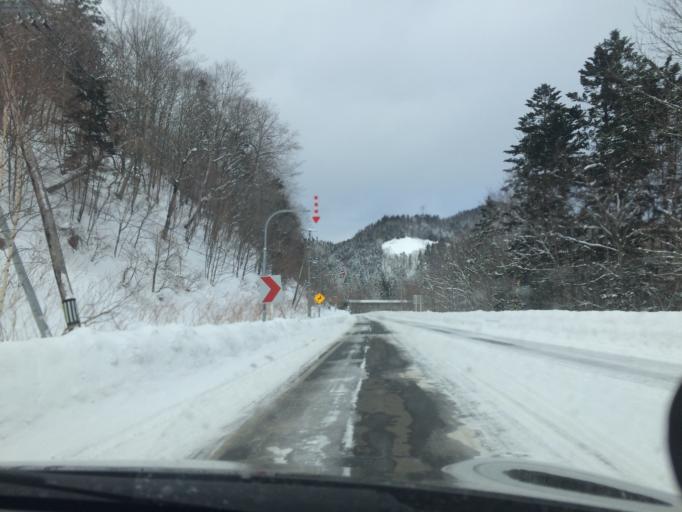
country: JP
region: Hokkaido
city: Shimo-furano
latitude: 43.0482
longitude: 142.4816
